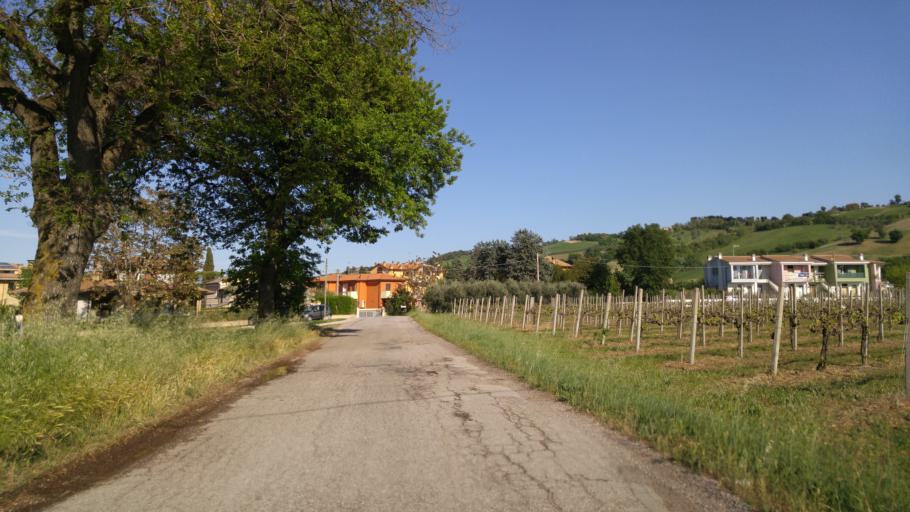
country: IT
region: The Marches
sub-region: Provincia di Pesaro e Urbino
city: Montemaggiore al Metauro
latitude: 43.7479
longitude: 12.9477
